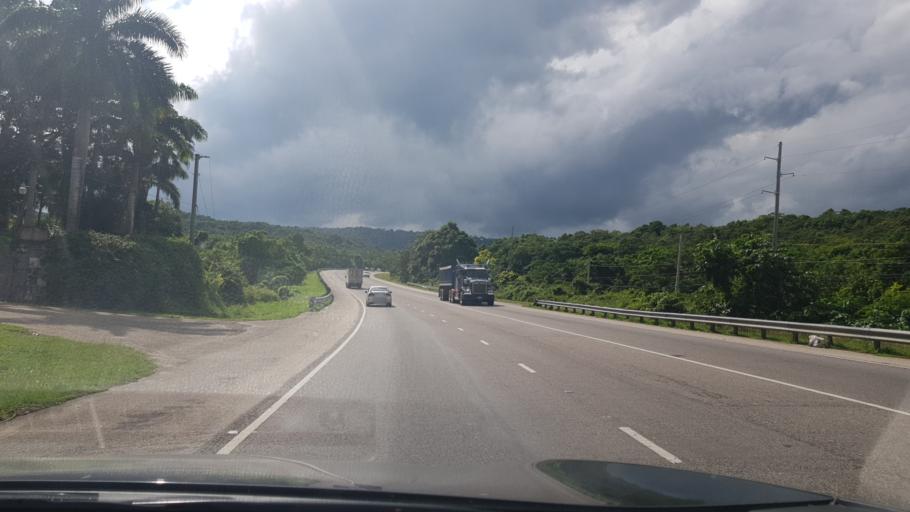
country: JM
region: Trelawny
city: Duncans
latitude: 18.4690
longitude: -77.4960
